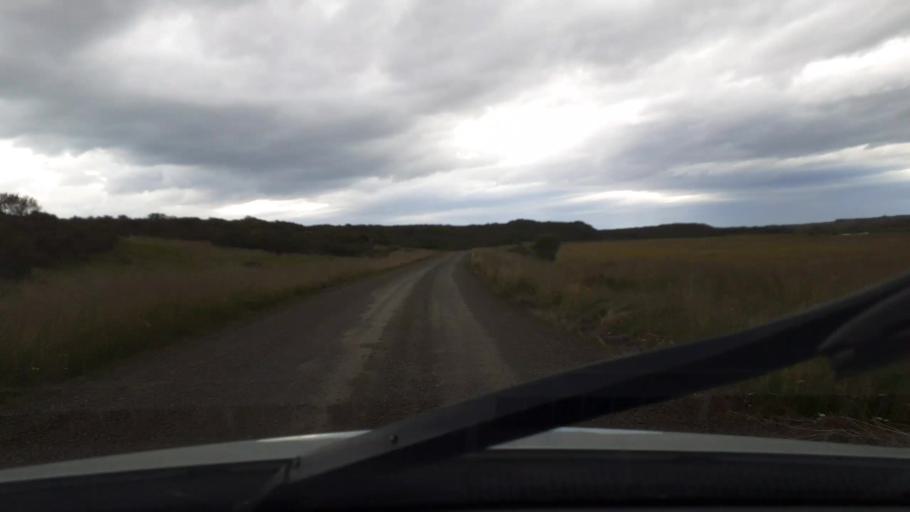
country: IS
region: West
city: Borgarnes
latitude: 64.6115
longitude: -21.9533
